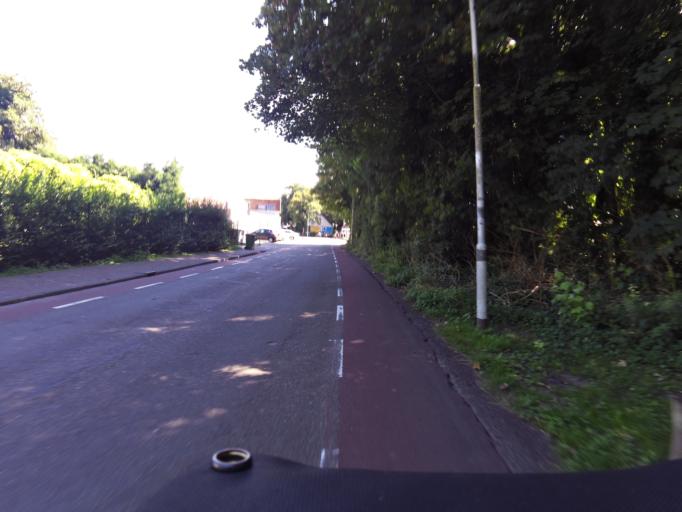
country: NL
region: Zeeland
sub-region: Schouwen-Duiveland
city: Renesse
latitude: 51.7319
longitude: 3.7710
